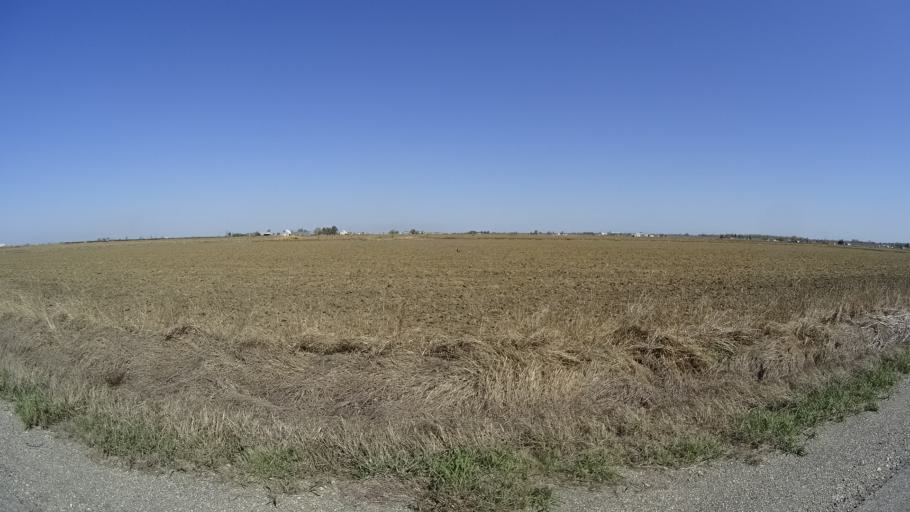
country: US
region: California
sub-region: Glenn County
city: Willows
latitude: 39.4285
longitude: -122.0384
